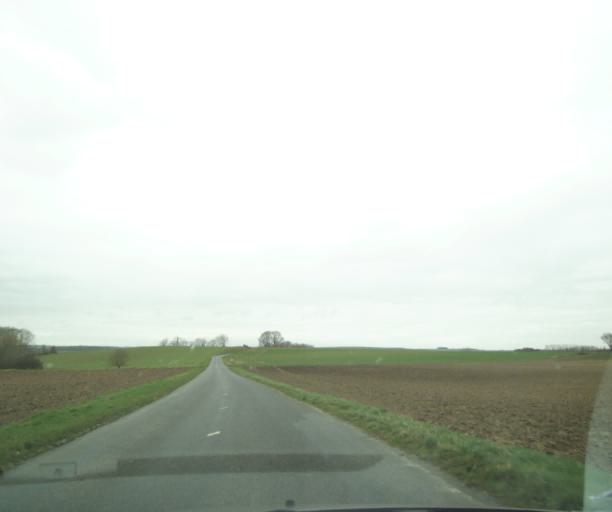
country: FR
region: Picardie
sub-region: Departement de l'Oise
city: Crisolles
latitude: 49.6042
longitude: 3.0081
